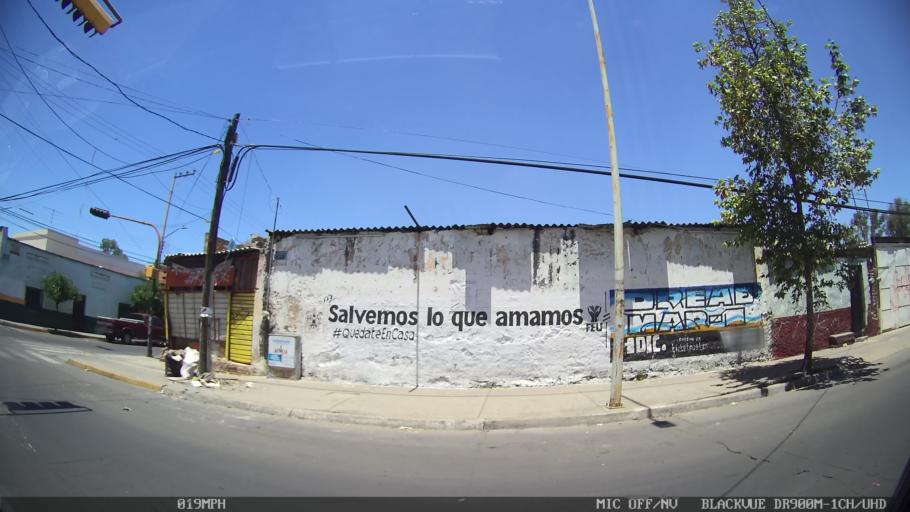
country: MX
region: Jalisco
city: Tlaquepaque
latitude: 20.6597
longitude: -103.2773
